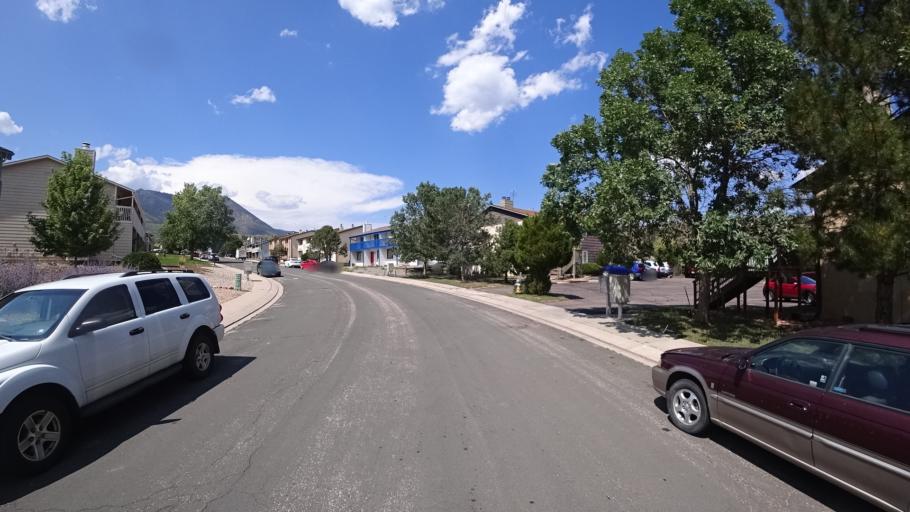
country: US
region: Colorado
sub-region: El Paso County
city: Air Force Academy
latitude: 38.9318
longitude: -104.8701
